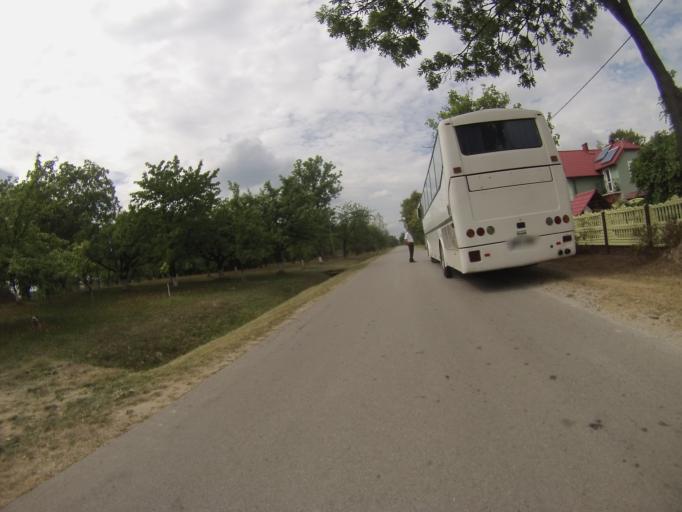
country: PL
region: Swietokrzyskie
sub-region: Powiat kielecki
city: Lagow
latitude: 50.7448
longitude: 21.0939
